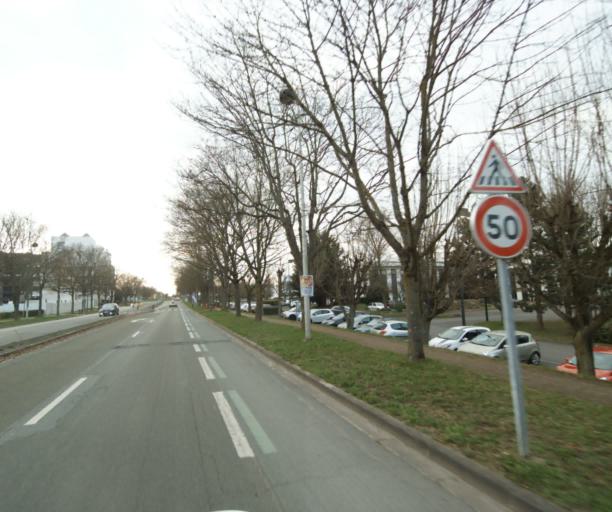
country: FR
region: Ile-de-France
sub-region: Departement du Val-d'Oise
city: Vaureal
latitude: 49.0531
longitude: 2.0354
